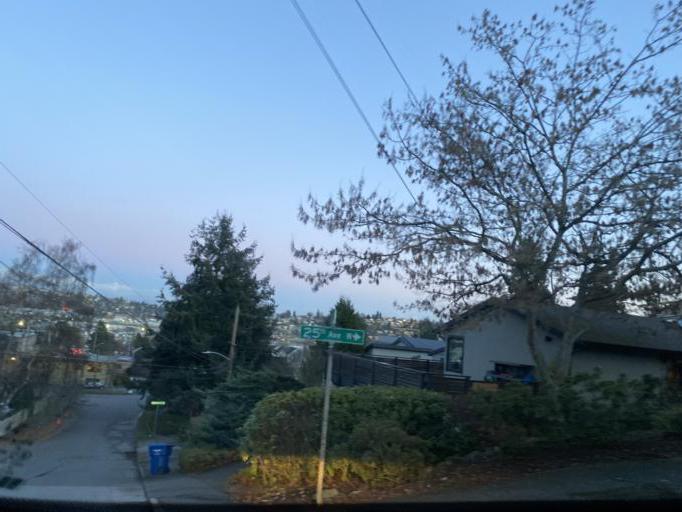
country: US
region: Washington
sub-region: King County
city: Seattle
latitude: 47.6559
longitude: -122.3887
